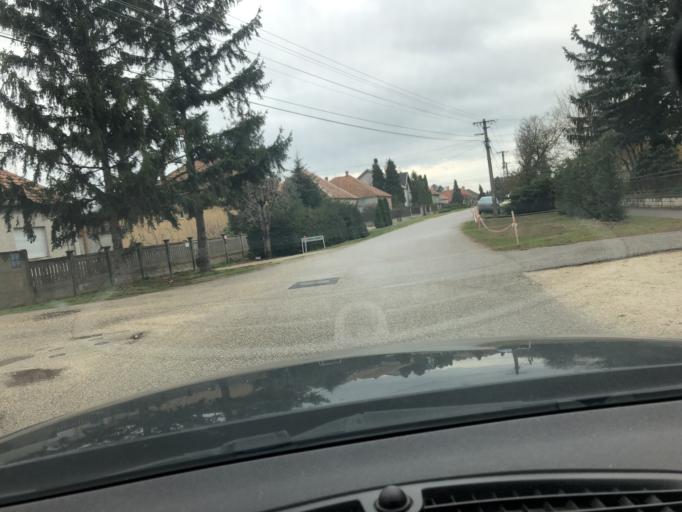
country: HU
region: Gyor-Moson-Sopron
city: Fertod
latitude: 47.6223
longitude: 16.8633
